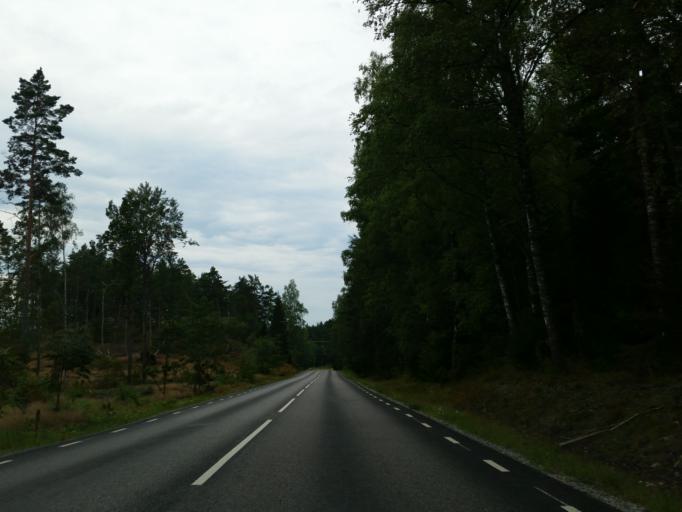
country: SE
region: Stockholm
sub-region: Salems Kommun
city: Ronninge
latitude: 59.2287
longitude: 17.6877
